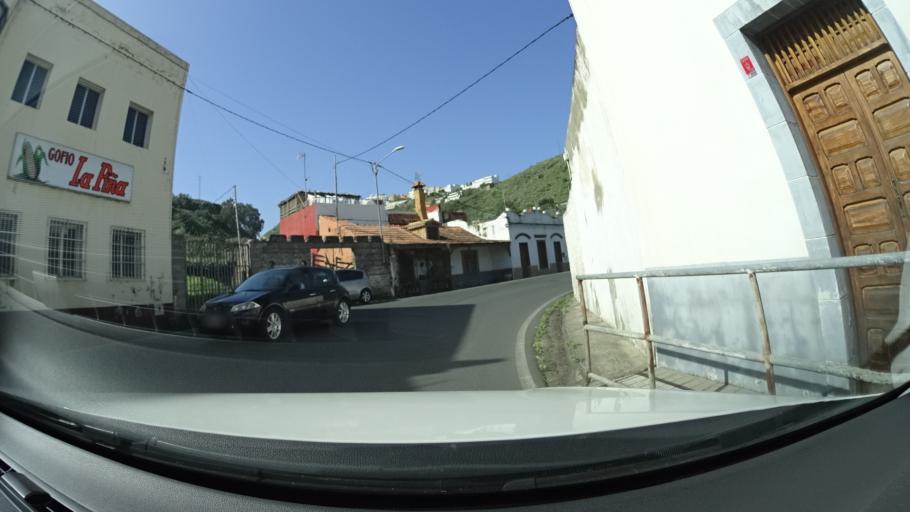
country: ES
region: Canary Islands
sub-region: Provincia de Las Palmas
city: Teror
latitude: 28.0685
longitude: -15.5269
